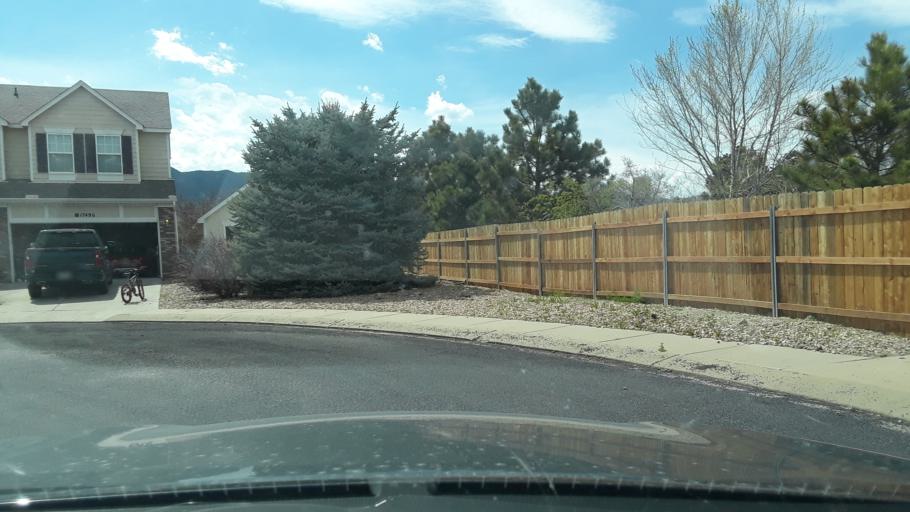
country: US
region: Colorado
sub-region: El Paso County
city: Monument
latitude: 39.0857
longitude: -104.8705
